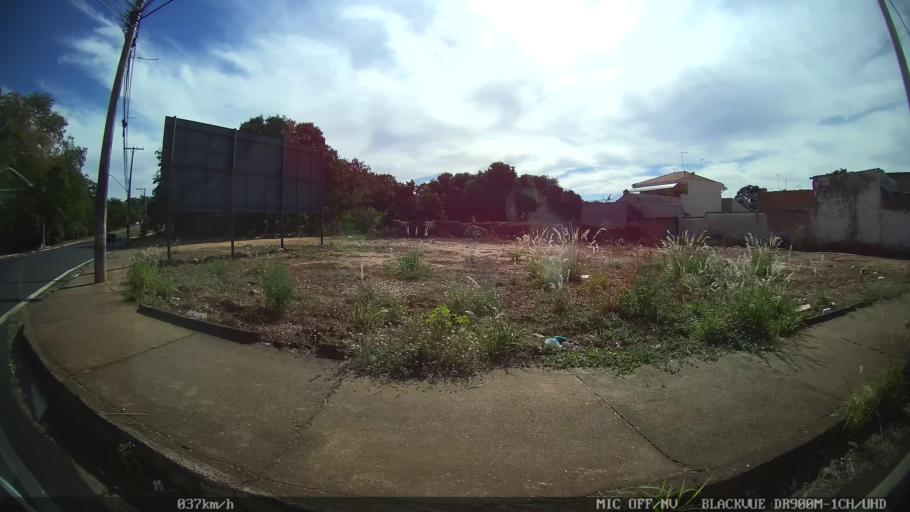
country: BR
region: Sao Paulo
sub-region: Catanduva
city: Catanduva
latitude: -21.1239
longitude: -48.9772
